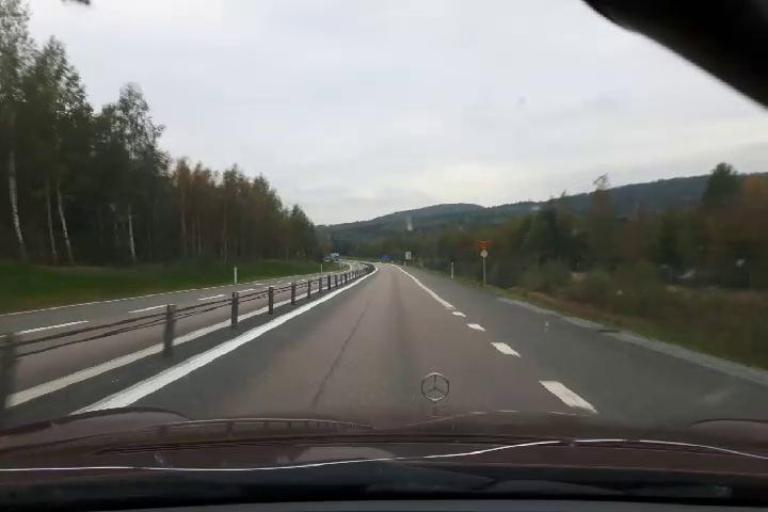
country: SE
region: Vaesternorrland
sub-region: Haernoesands Kommun
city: Haernoesand
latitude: 62.8731
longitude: 18.0476
